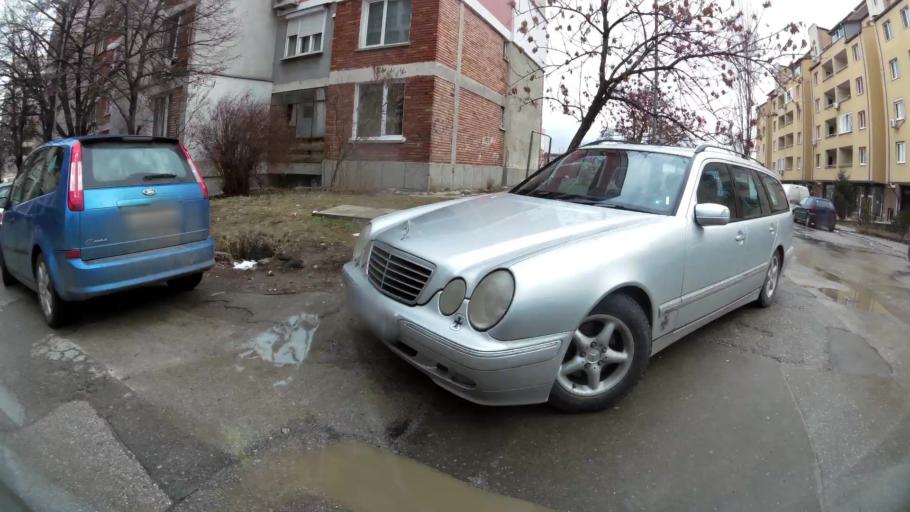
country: BG
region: Sofiya
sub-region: Obshtina Bozhurishte
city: Bozhurishte
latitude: 42.7228
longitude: 23.2519
